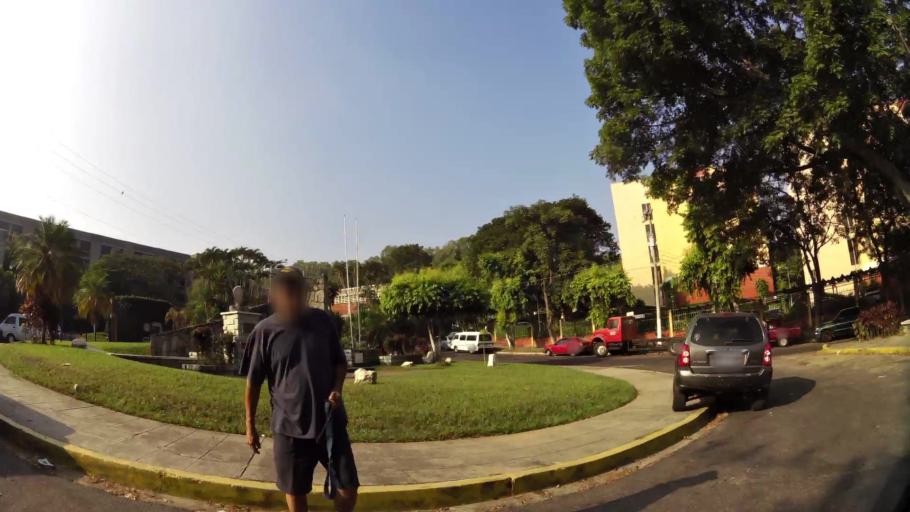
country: SV
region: San Salvador
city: San Salvador
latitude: 13.6817
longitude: -89.2187
